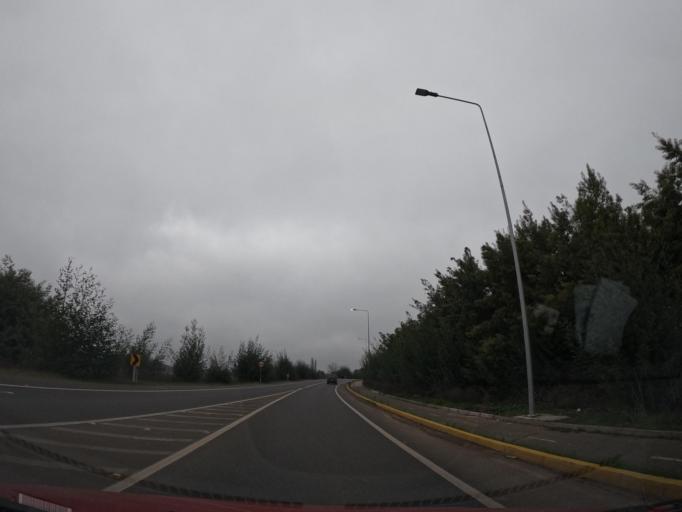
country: CL
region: Maule
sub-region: Provincia de Talca
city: San Clemente
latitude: -35.5291
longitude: -71.4761
